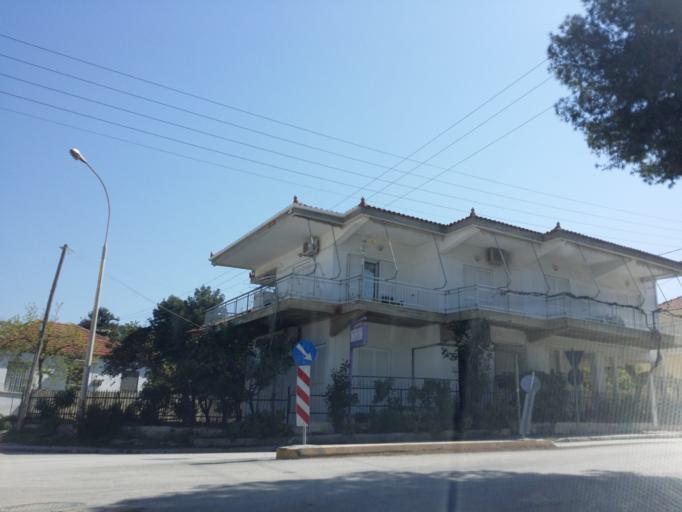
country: GR
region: Peloponnese
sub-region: Nomos Korinthias
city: Xylokastro
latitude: 38.0746
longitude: 22.6204
